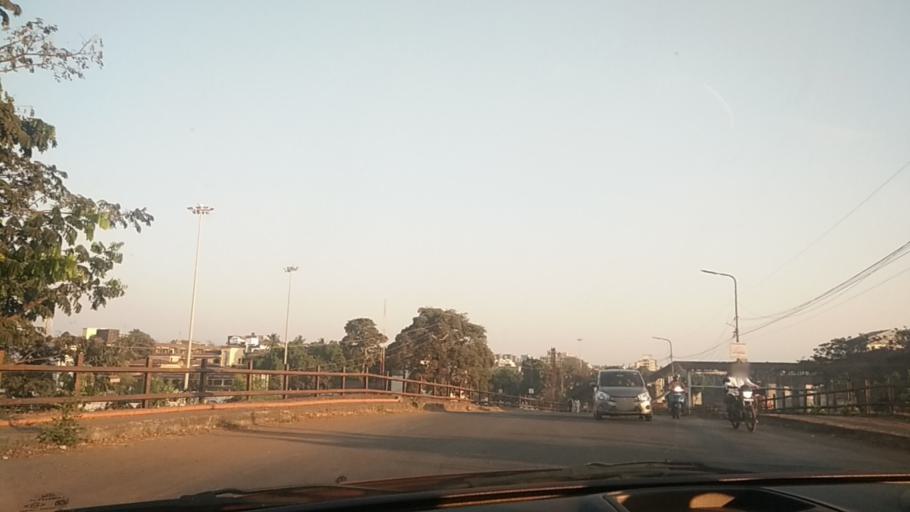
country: IN
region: Goa
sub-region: South Goa
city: Vasco Da Gama
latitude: 15.3979
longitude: 73.8055
